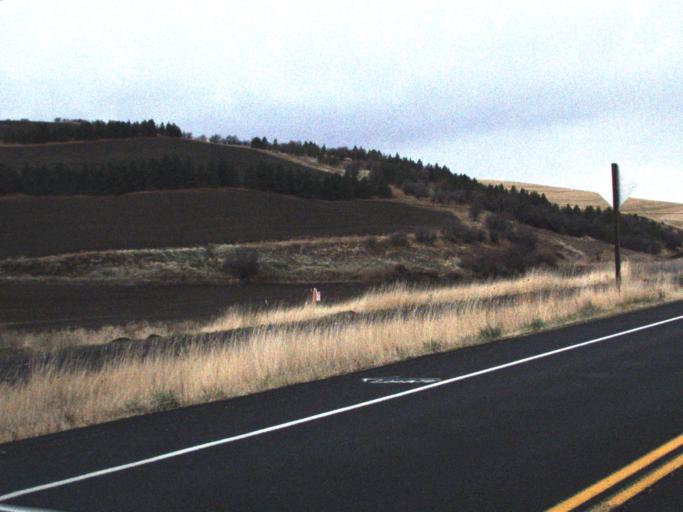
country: US
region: Washington
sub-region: Columbia County
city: Dayton
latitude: 46.3293
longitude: -117.9757
